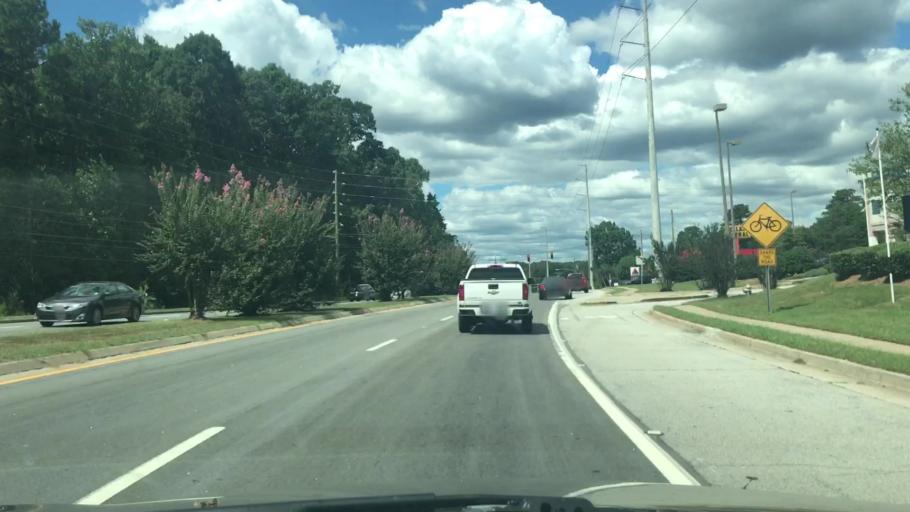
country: US
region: Georgia
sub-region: Gwinnett County
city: Mountain Park
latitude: 33.8092
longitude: -84.0971
